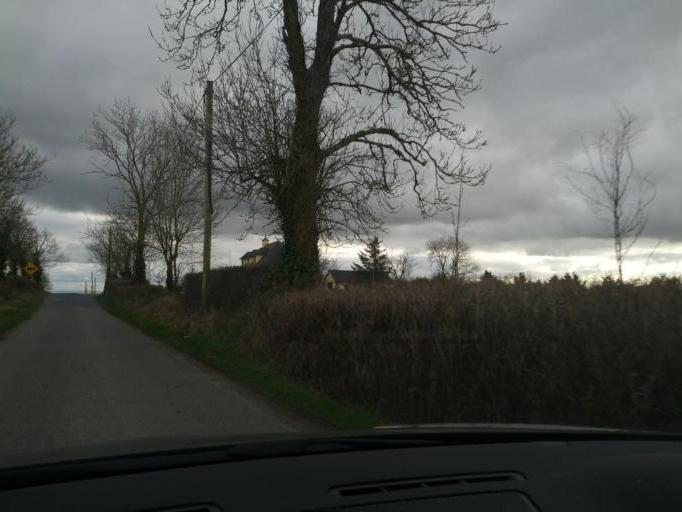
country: IE
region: Leinster
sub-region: Uibh Fhaili
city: Clara
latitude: 53.4010
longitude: -7.6205
